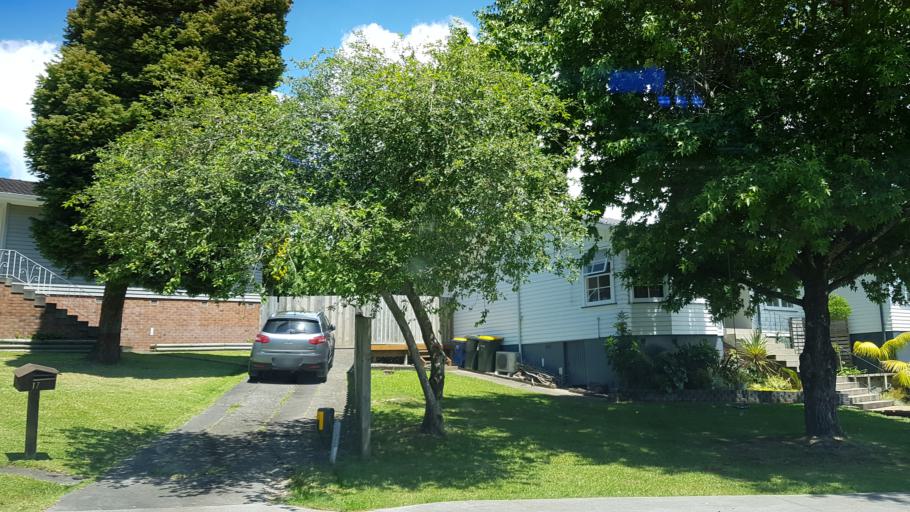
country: NZ
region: Auckland
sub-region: Auckland
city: North Shore
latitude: -36.7943
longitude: 174.6990
